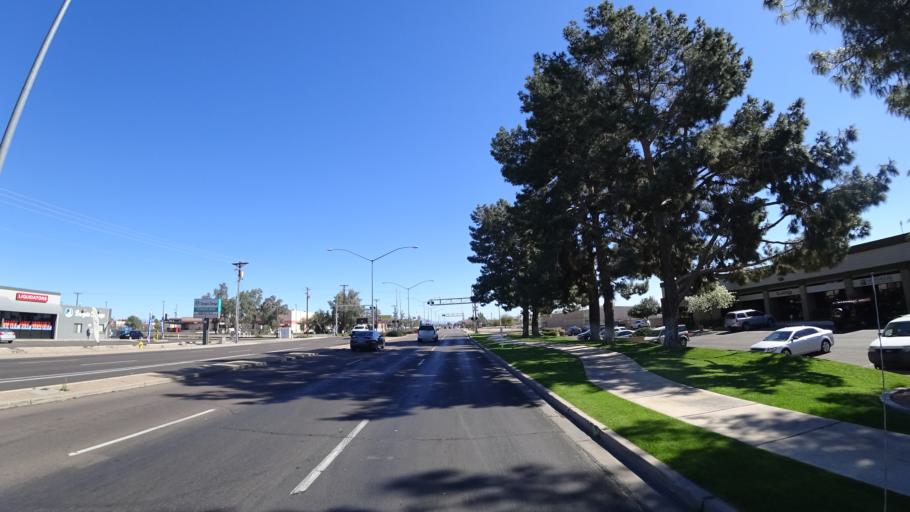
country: US
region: Arizona
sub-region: Maricopa County
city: San Carlos
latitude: 33.3787
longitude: -111.8326
